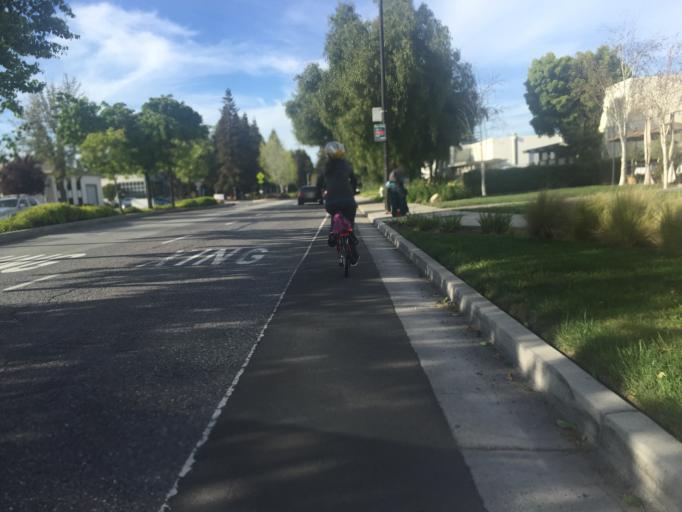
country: US
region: California
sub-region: Santa Clara County
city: Mountain View
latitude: 37.4158
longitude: -122.0779
